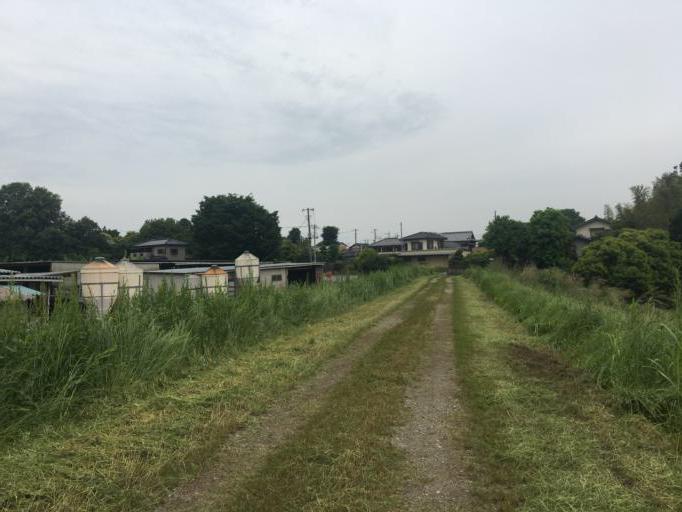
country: JP
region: Saitama
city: Sakado
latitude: 36.0145
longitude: 139.4388
